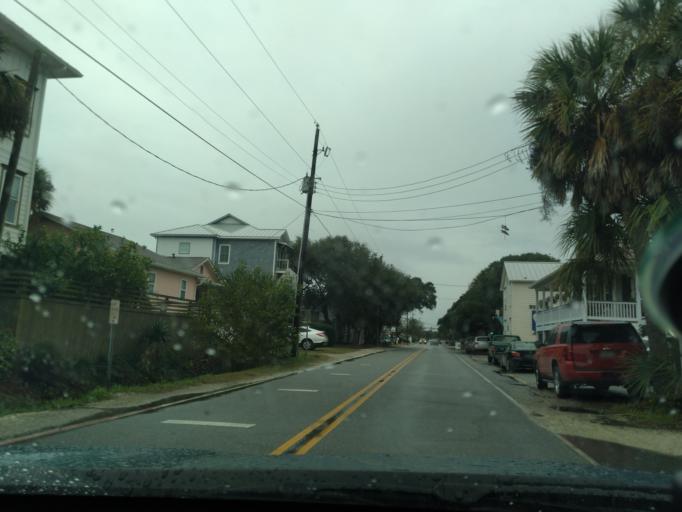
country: US
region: South Carolina
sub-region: Charleston County
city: Folly Beach
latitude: 32.6564
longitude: -79.9386
